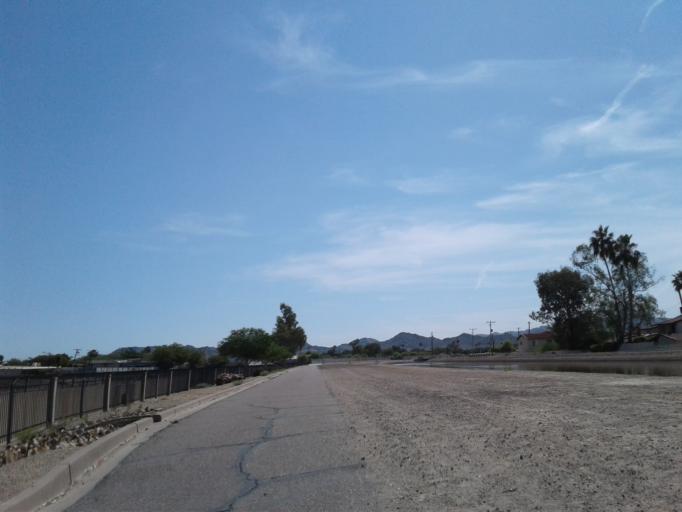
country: US
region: Arizona
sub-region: Maricopa County
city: Glendale
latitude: 33.5687
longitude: -112.0856
